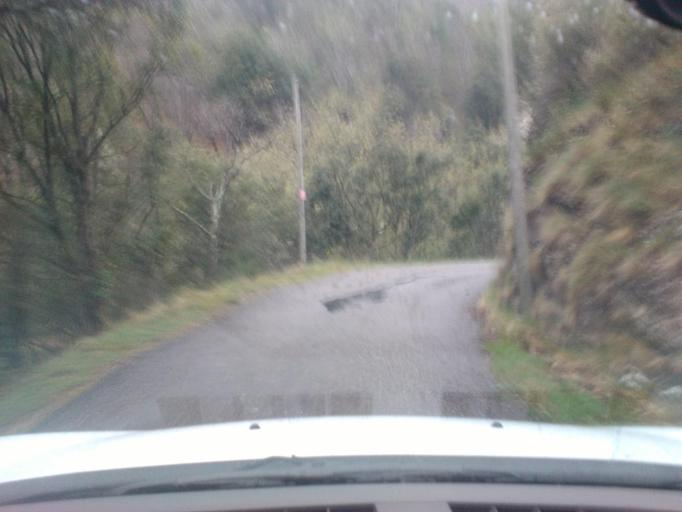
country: FR
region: Languedoc-Roussillon
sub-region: Departement du Gard
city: Valleraugue
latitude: 44.1085
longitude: 3.6698
